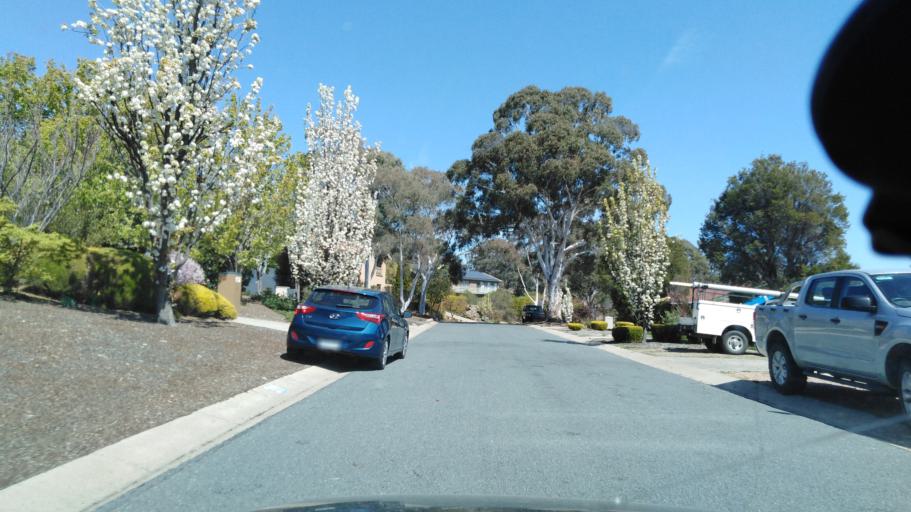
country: AU
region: Australian Capital Territory
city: Macquarie
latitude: -35.3495
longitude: 149.0256
